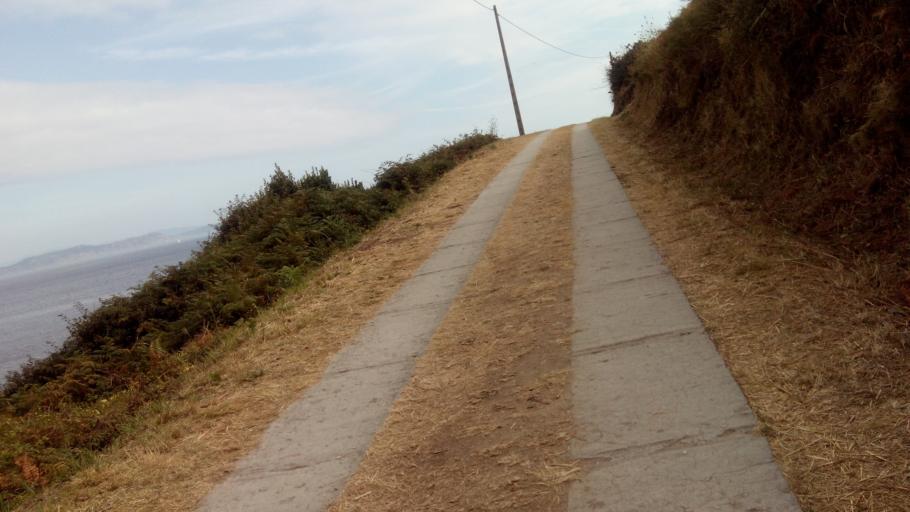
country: ES
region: Galicia
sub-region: Provincia de Pontevedra
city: Sanxenxo
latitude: 42.3677
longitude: -8.9348
